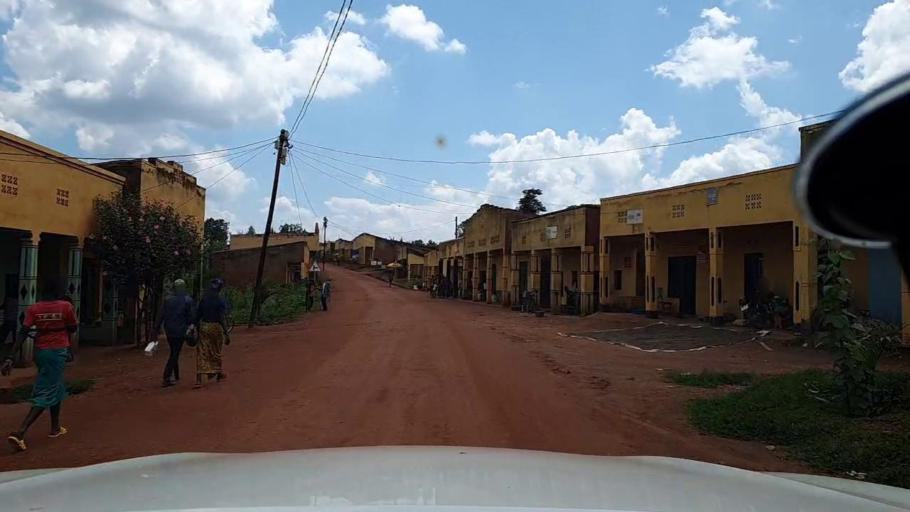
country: RW
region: Kigali
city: Kigali
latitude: -1.8039
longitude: 29.8417
